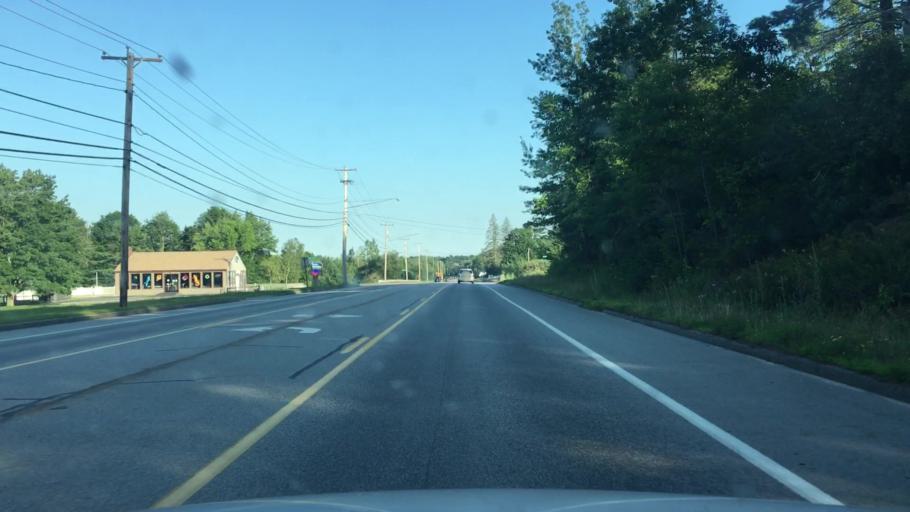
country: US
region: Maine
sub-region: Androscoggin County
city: Lisbon
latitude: 44.0586
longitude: -70.1443
